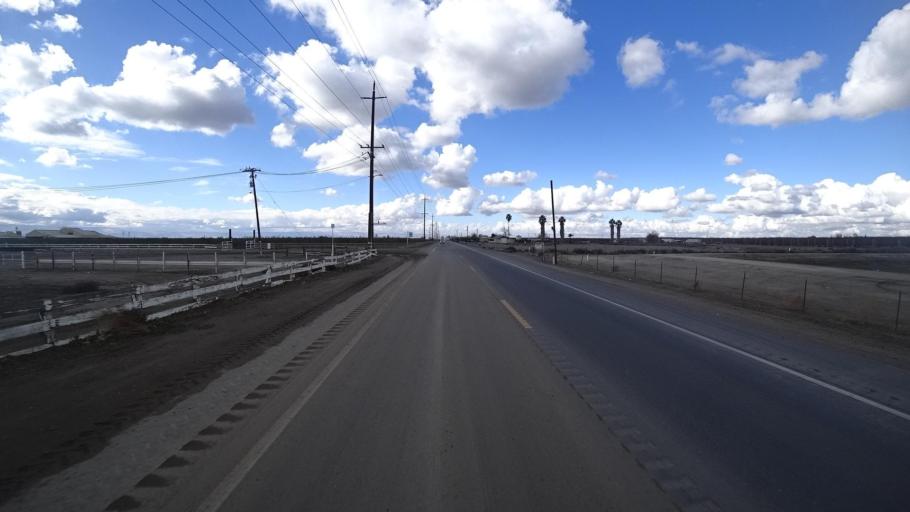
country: US
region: California
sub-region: Kern County
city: Greenfield
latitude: 35.2087
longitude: -119.0866
